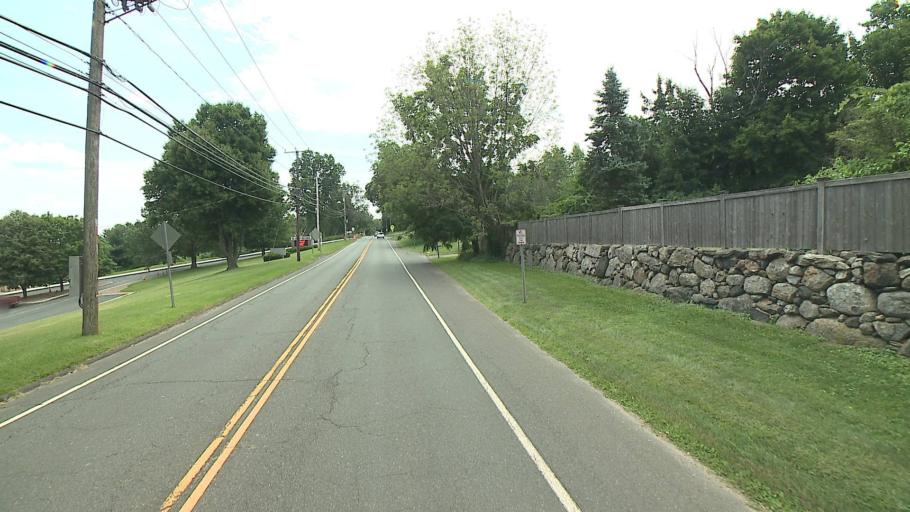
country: US
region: Connecticut
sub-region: Fairfield County
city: Danbury
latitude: 41.4161
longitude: -73.4724
